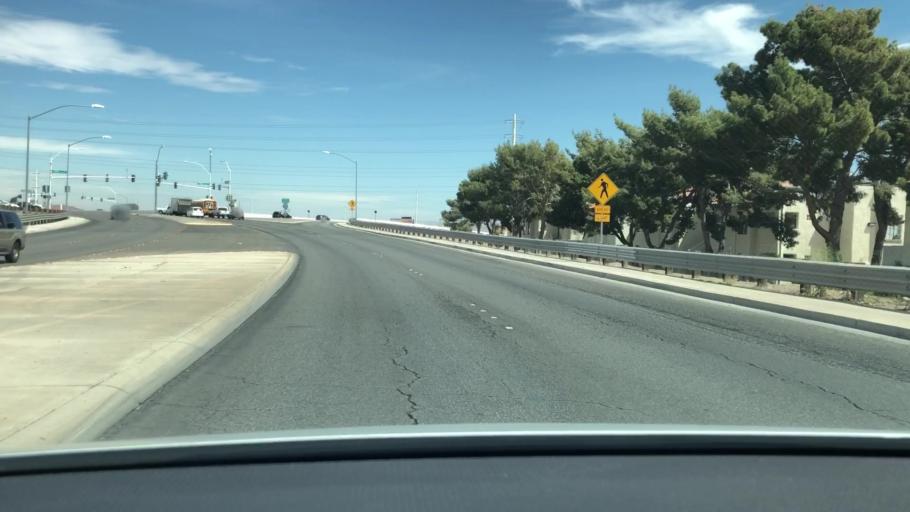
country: US
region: Nevada
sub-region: Clark County
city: Whitney
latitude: 36.0821
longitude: -115.0525
